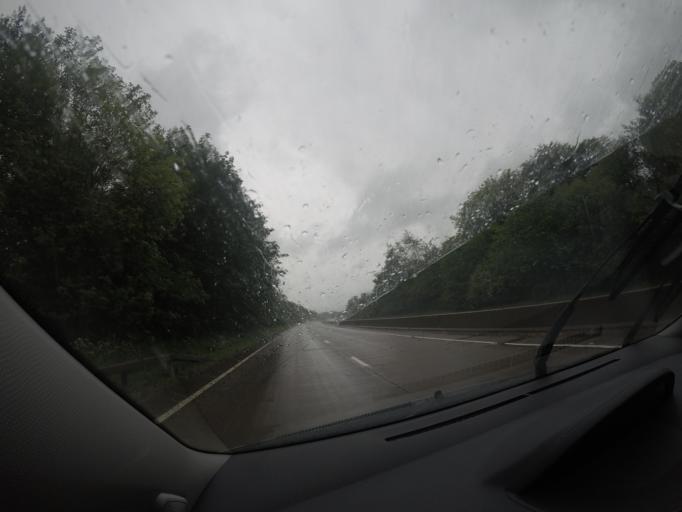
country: GB
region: Scotland
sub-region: Angus
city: Brechin
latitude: 56.7312
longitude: -2.6933
